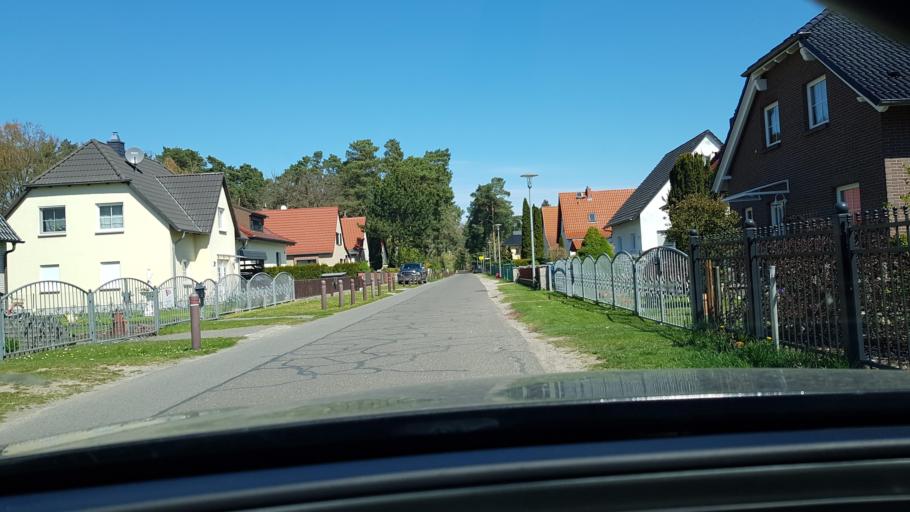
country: DE
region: Brandenburg
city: Rangsdorf
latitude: 52.3408
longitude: 13.4029
